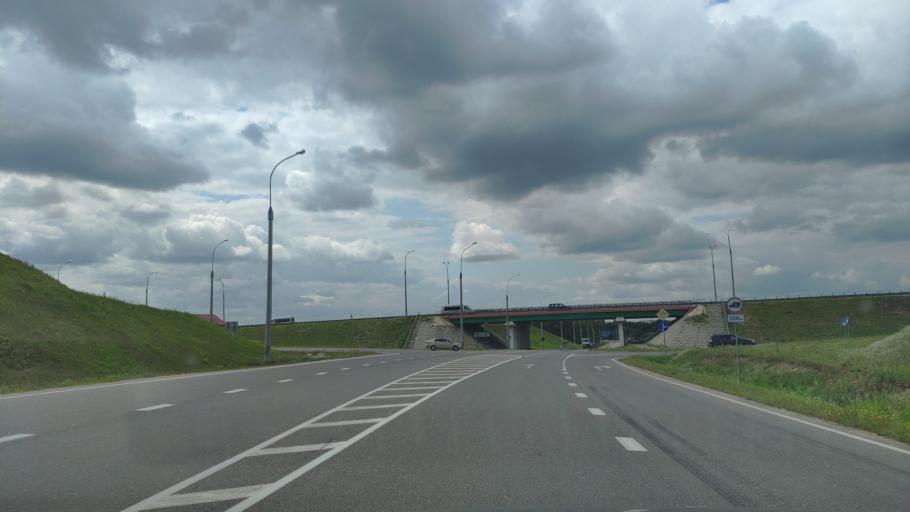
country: BY
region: Minsk
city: Zaslawye
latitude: 54.0061
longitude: 27.3114
